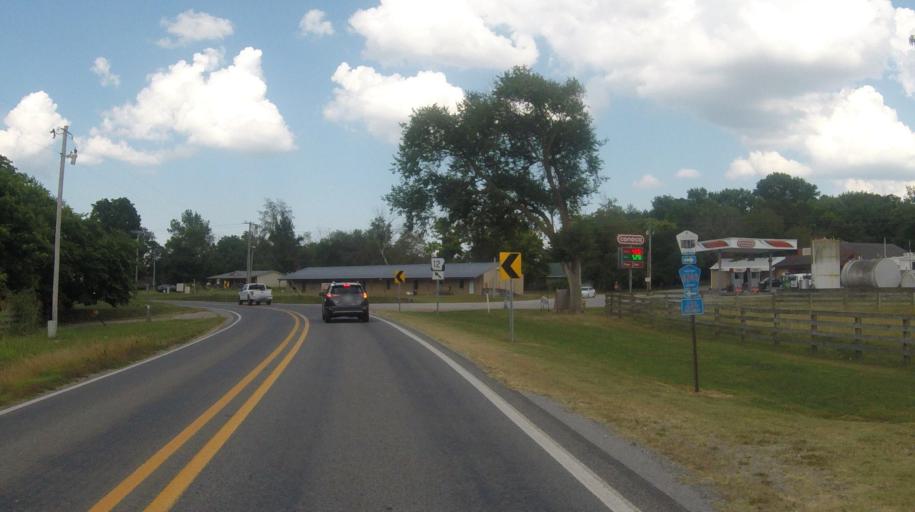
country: US
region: Arkansas
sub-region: Madison County
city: Huntsville
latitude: 36.2358
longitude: -93.7990
